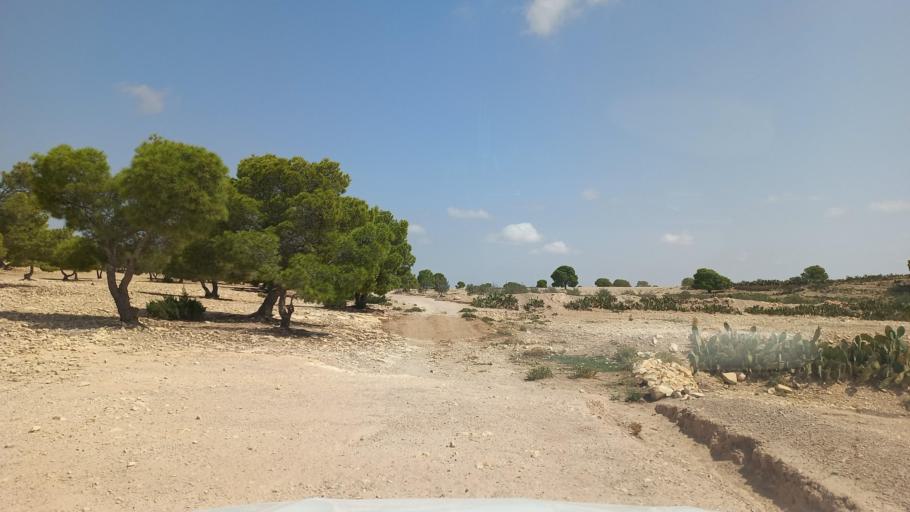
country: TN
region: Al Qasrayn
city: Sbiba
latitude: 35.4059
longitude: 8.9698
